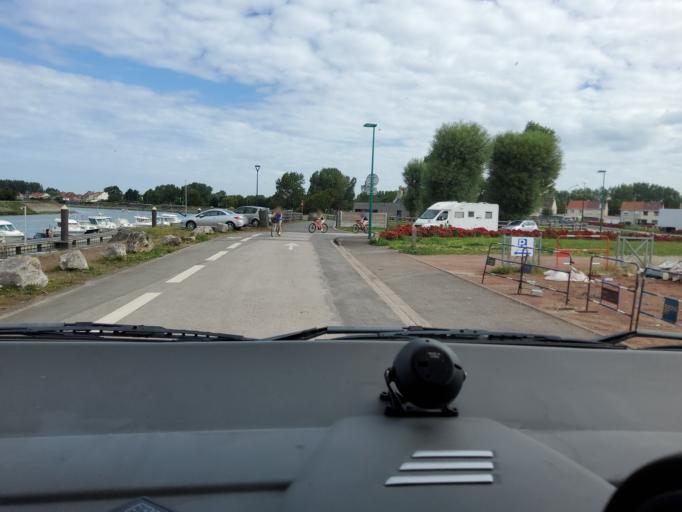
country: FR
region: Nord-Pas-de-Calais
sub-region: Departement du Nord
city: Gravelines
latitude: 50.9888
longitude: 2.1227
